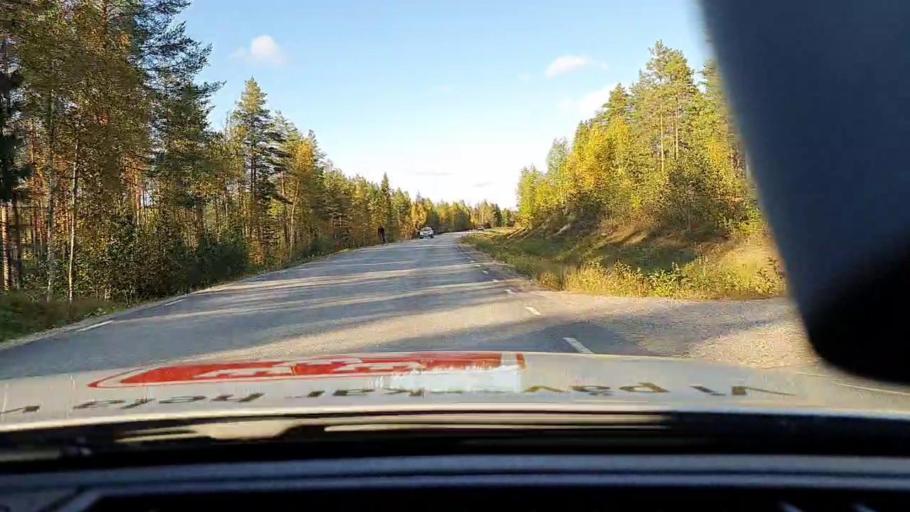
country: SE
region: Norrbotten
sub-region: Pitea Kommun
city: Norrfjarden
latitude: 65.4994
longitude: 21.4757
